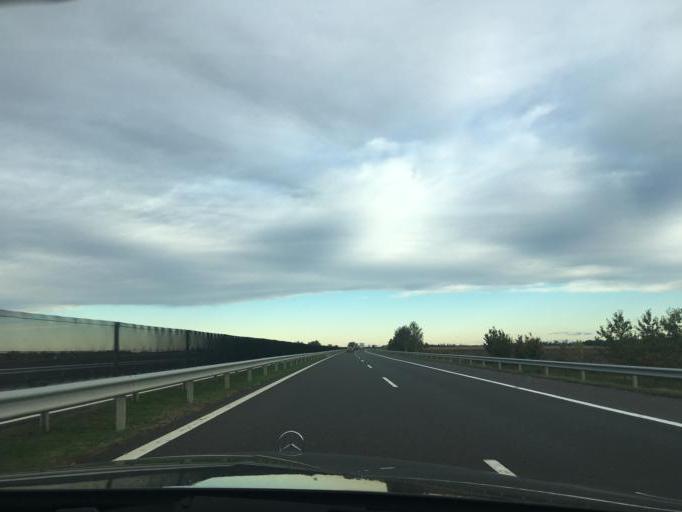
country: HU
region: Hajdu-Bihar
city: Hajduboszormeny
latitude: 47.6928
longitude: 21.4430
